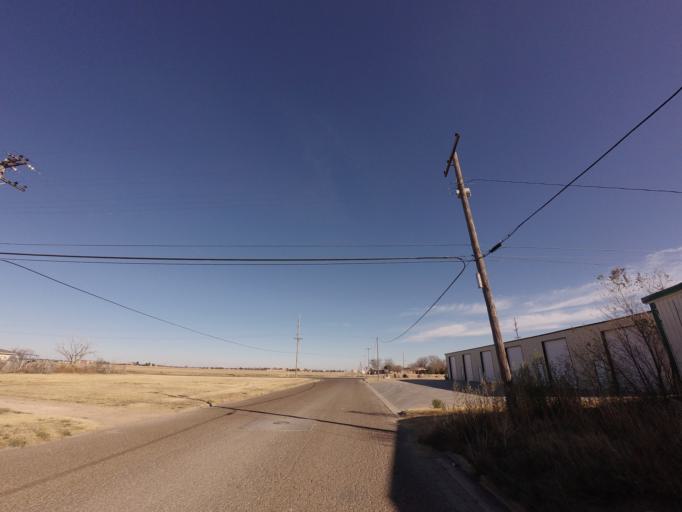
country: US
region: New Mexico
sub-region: Curry County
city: Clovis
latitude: 34.3997
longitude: -103.1796
